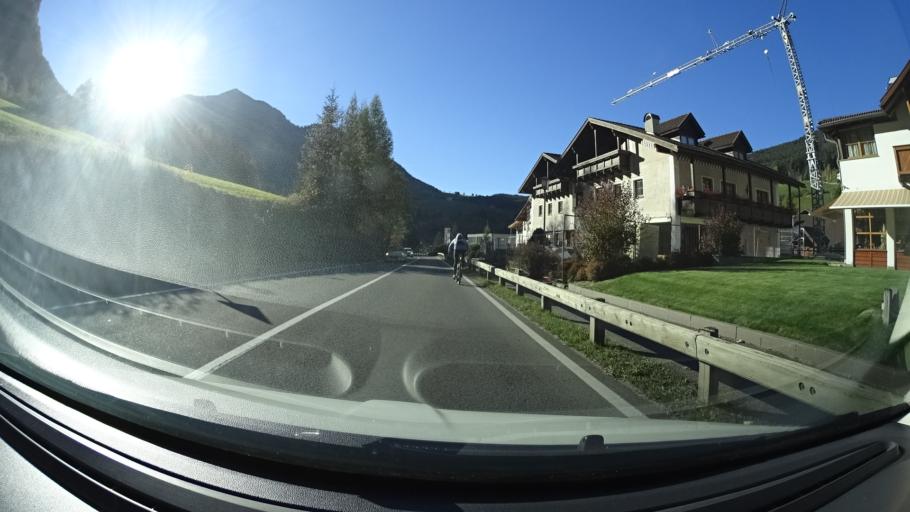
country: IT
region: Trentino-Alto Adige
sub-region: Bolzano
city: Ortisei
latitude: 46.5734
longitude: 11.6542
